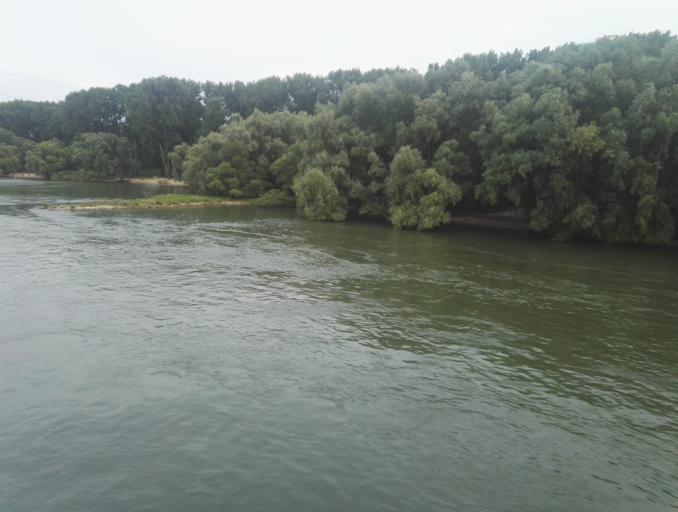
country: DE
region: North Rhine-Westphalia
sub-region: Regierungsbezirk Koln
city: Poll
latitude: 50.8937
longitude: 7.0105
